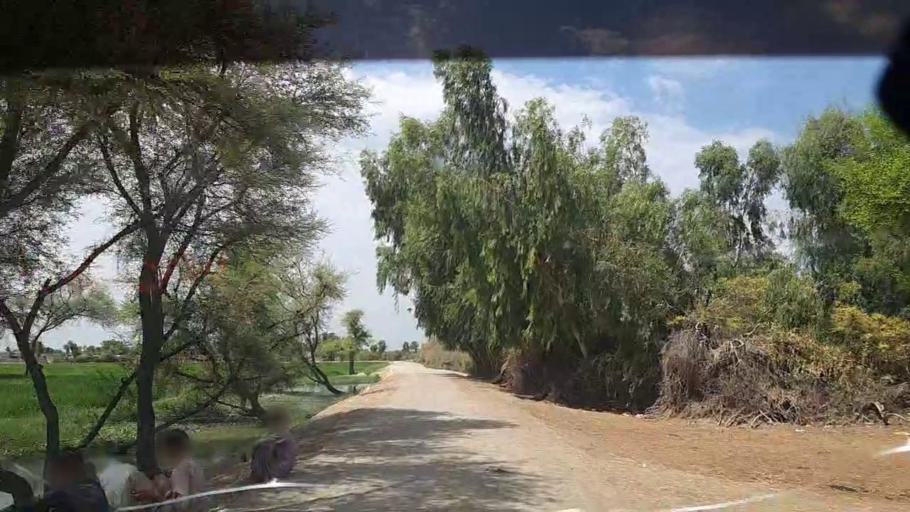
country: PK
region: Sindh
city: Ghauspur
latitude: 28.1521
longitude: 68.9975
